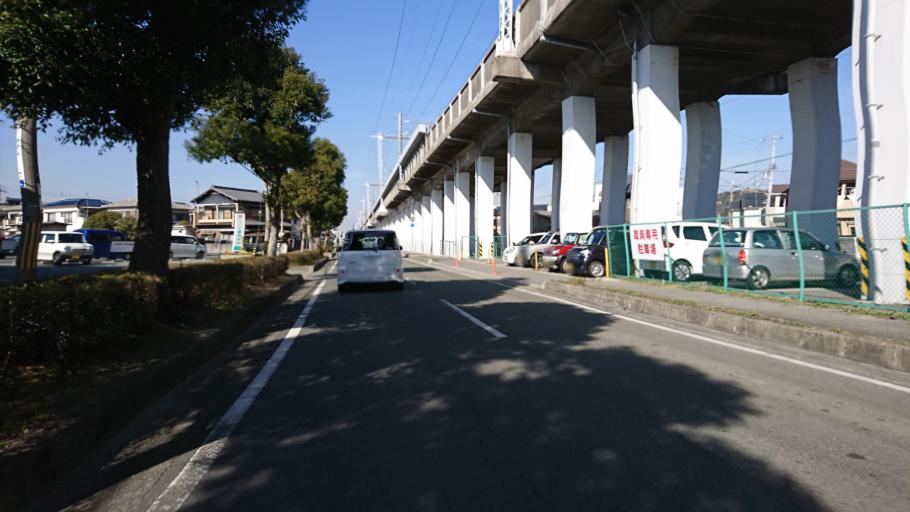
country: JP
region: Hyogo
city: Kakogawacho-honmachi
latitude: 34.7671
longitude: 134.7986
